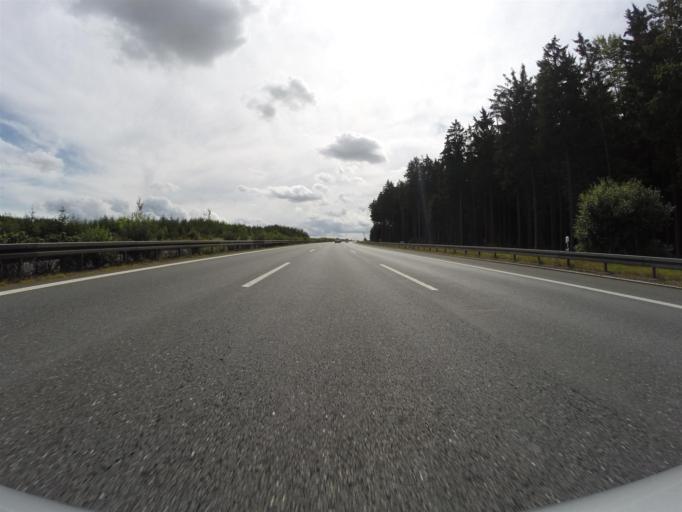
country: DE
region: Bavaria
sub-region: Upper Franconia
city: Leupoldsgrun
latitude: 50.2502
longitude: 11.7913
